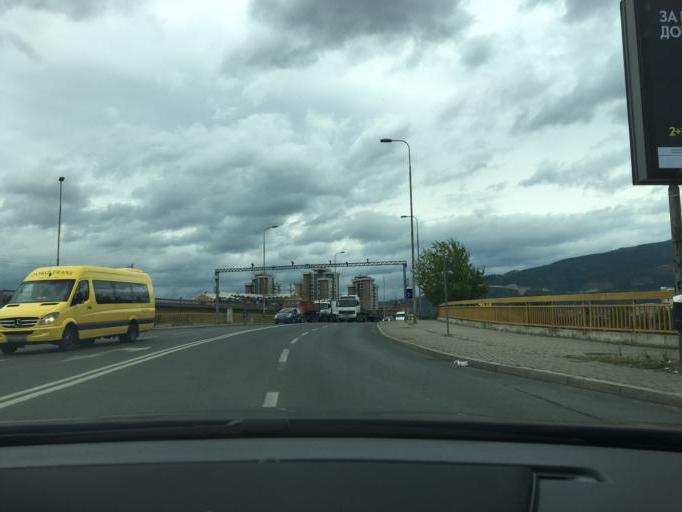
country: MK
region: Karpos
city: Skopje
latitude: 41.9963
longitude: 21.4499
